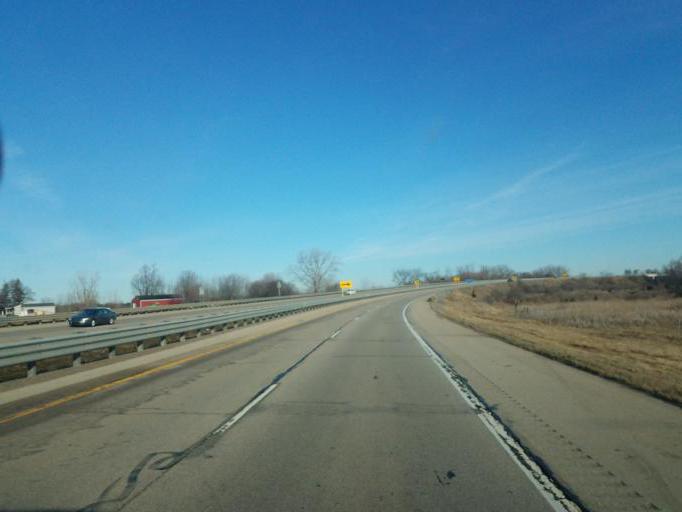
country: US
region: Michigan
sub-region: Gratiot County
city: Ithaca
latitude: 43.2826
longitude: -84.5796
